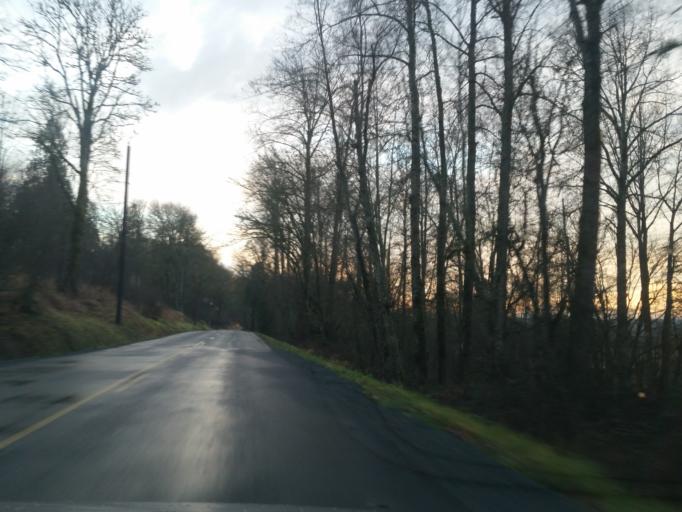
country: US
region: Washington
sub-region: Snohomish County
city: Cathcart
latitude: 47.8559
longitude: -122.0934
